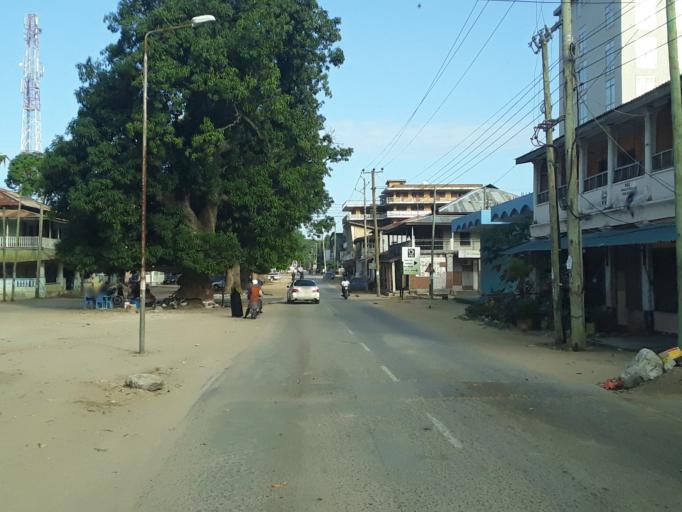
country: TZ
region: Tanga
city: Tanga
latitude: -5.0726
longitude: 39.1048
